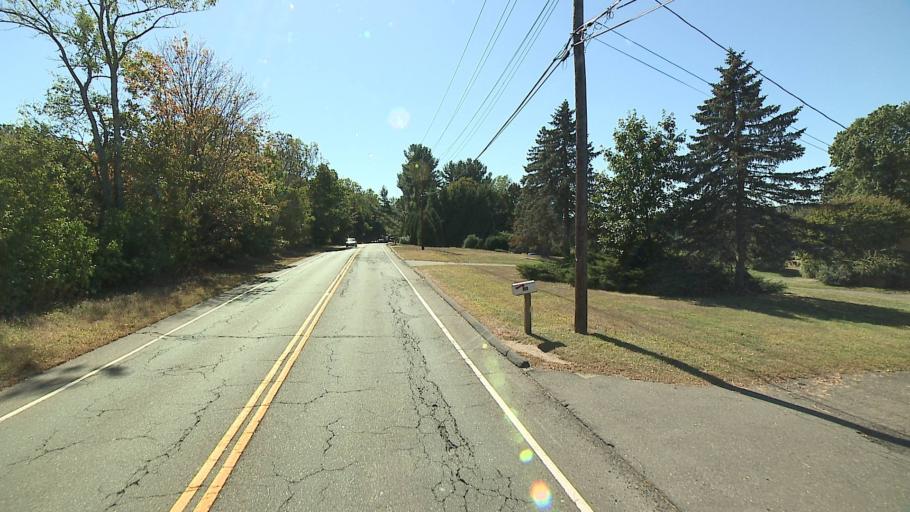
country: US
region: Connecticut
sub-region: New Haven County
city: Orange
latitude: 41.2807
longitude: -73.0409
